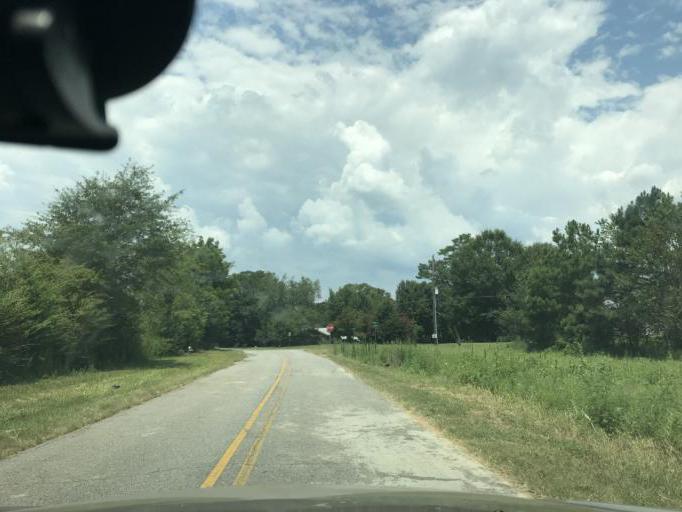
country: US
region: Georgia
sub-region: Dawson County
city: Dawsonville
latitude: 34.3343
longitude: -84.1308
